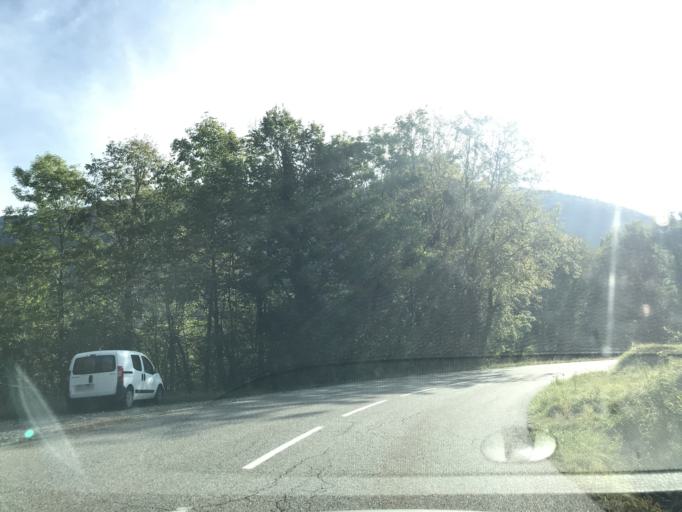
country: FR
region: Rhone-Alpes
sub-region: Departement de la Savoie
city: Yenne
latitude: 45.6626
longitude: 5.7893
